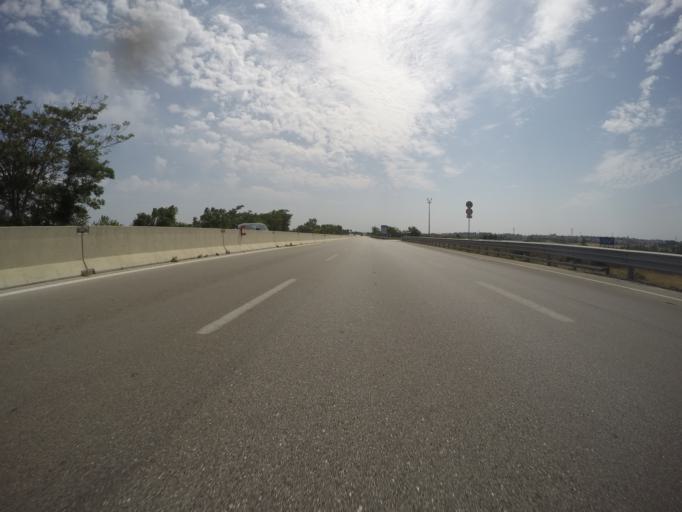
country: IT
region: Apulia
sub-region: Provincia di Brindisi
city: Francavilla Fontana
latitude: 40.5464
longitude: 17.5731
